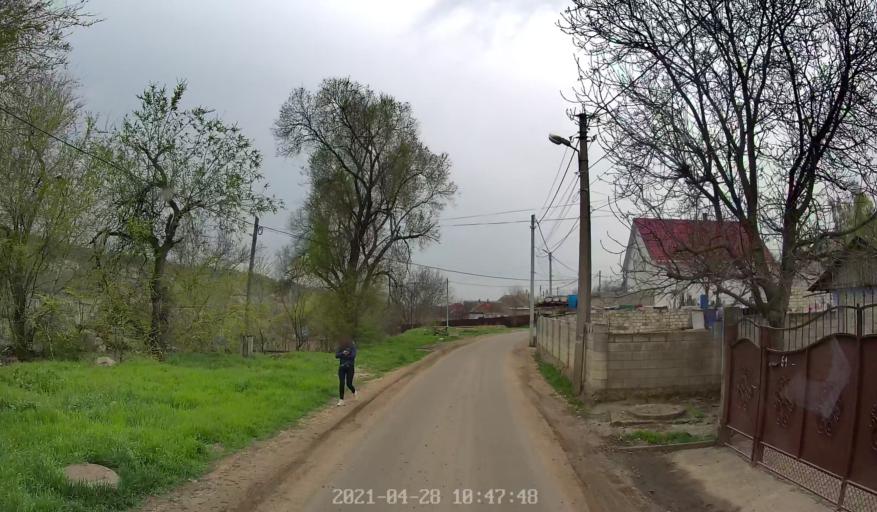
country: MD
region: Chisinau
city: Singera
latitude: 46.9871
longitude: 28.9468
